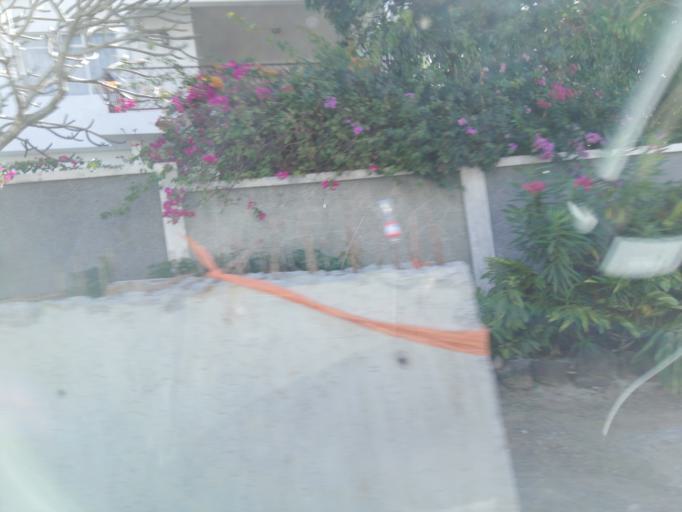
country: MU
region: Moka
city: Moka
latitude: -20.2254
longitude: 57.4747
